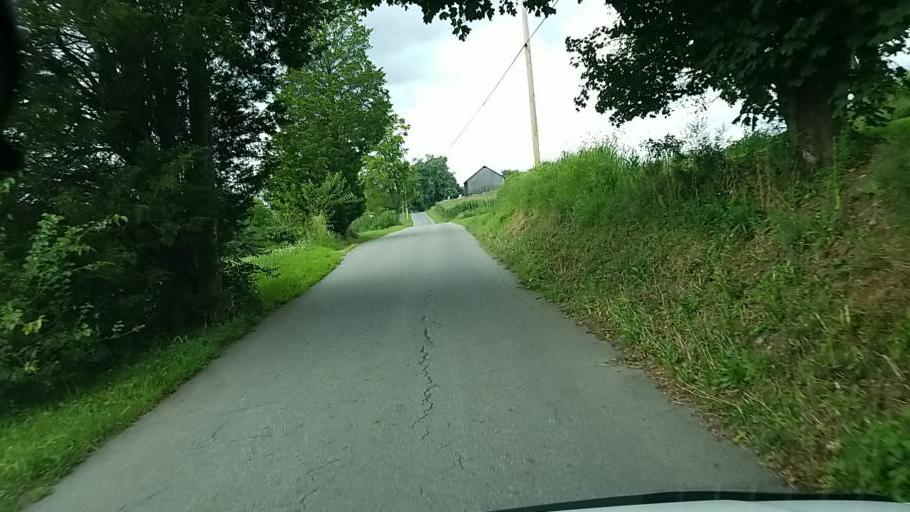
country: US
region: Pennsylvania
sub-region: Dauphin County
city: Elizabethville
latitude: 40.5972
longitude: -76.8029
